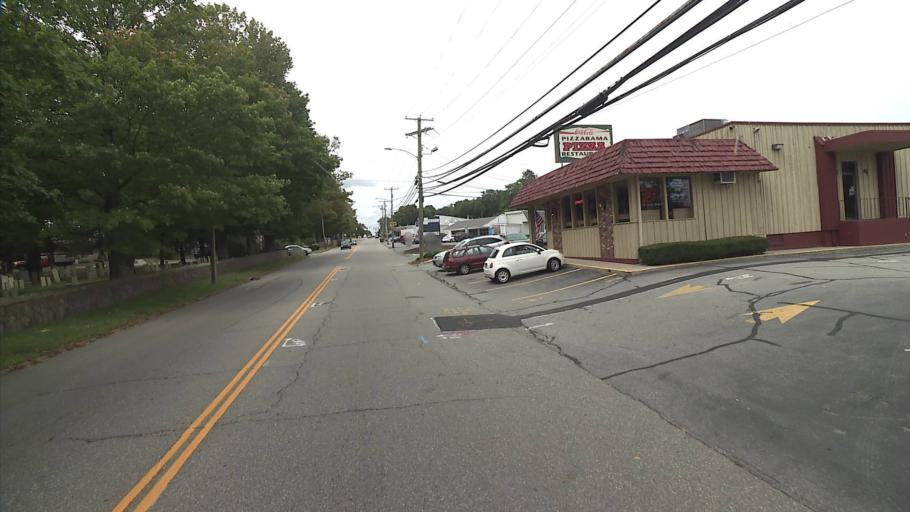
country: US
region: Connecticut
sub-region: New London County
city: Central Waterford
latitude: 41.3666
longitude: -72.1231
